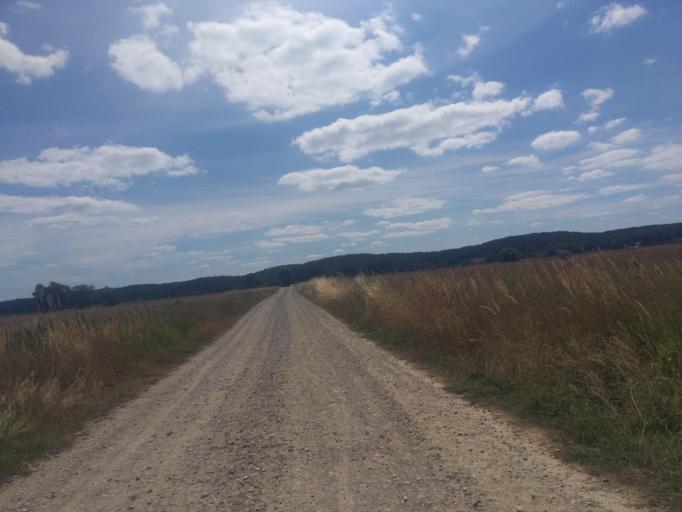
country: DE
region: Lower Saxony
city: Neu Darchau
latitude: 53.2482
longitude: 10.8523
